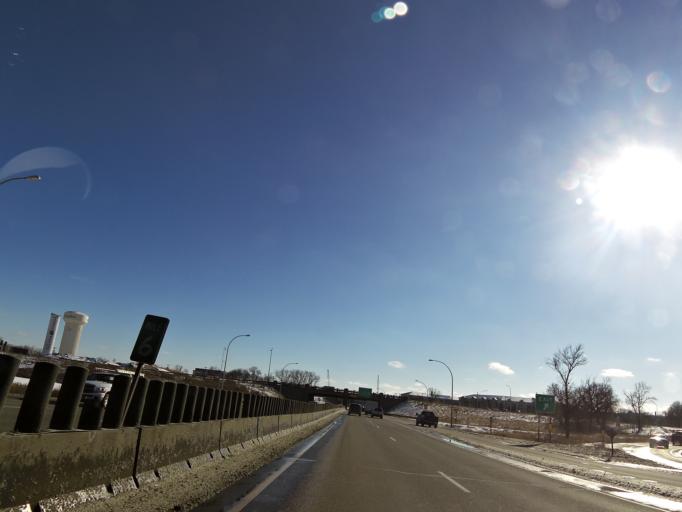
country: US
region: Minnesota
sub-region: Hennepin County
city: Saint Louis Park
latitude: 44.9456
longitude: -93.3480
